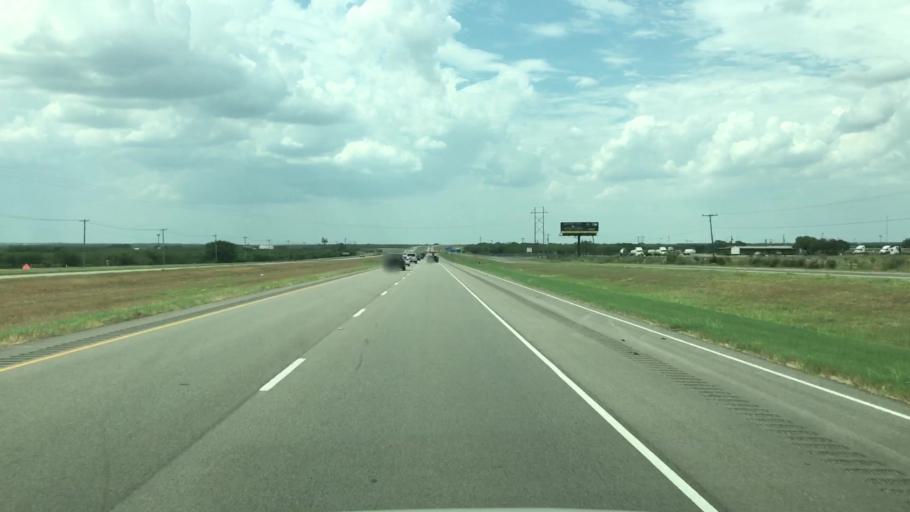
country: US
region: Texas
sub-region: Live Oak County
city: Three Rivers
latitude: 28.5115
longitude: -98.1694
